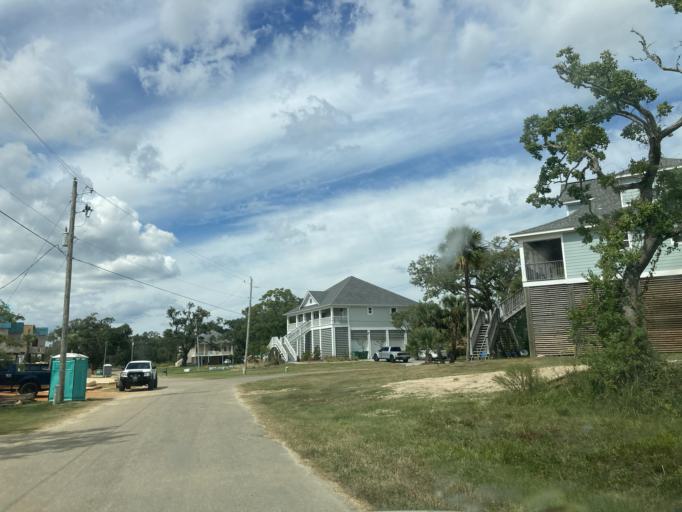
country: US
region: Mississippi
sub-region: Jackson County
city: Saint Martin
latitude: 30.4261
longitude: -88.8723
